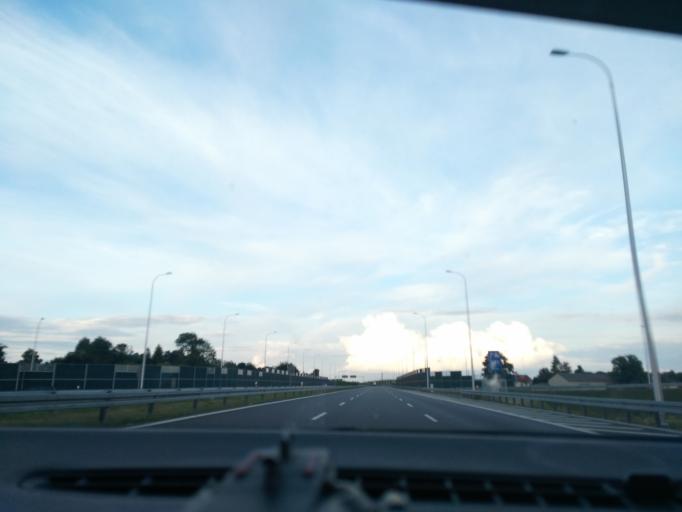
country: PL
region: Lublin Voivodeship
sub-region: Powiat lubelski
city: Lublin
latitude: 51.2999
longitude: 22.5168
